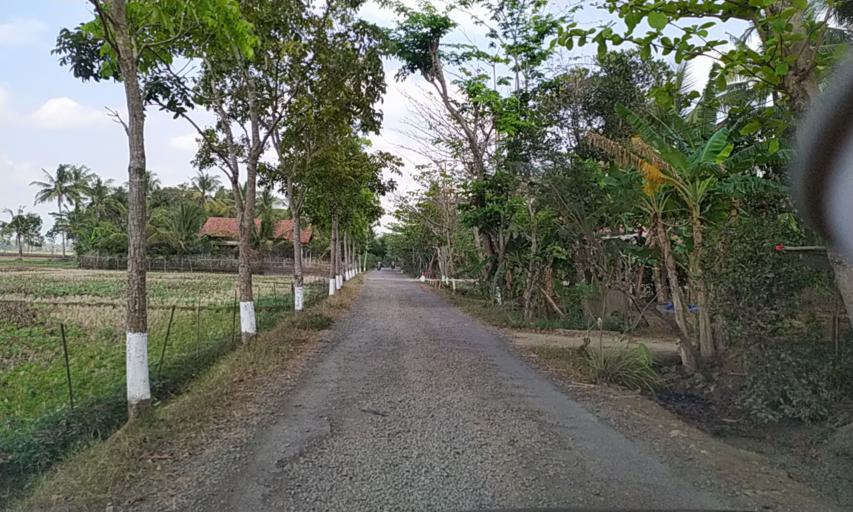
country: ID
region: Central Java
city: Tambaksari
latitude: -7.4888
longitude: 108.7551
